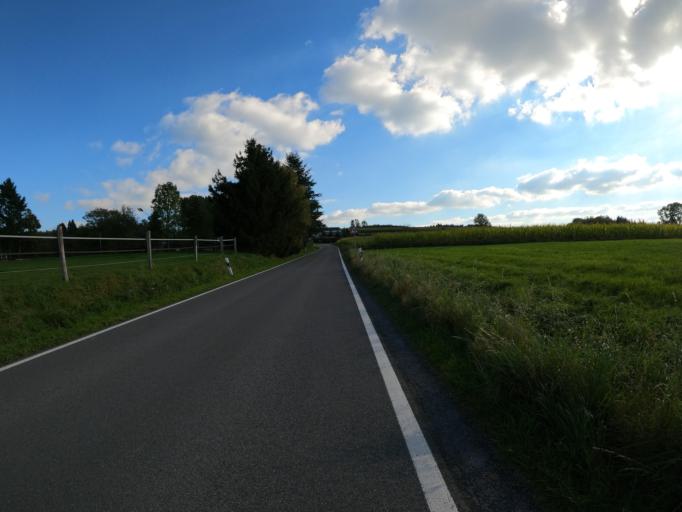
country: DE
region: North Rhine-Westphalia
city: Radevormwald
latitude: 51.2318
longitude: 7.3368
